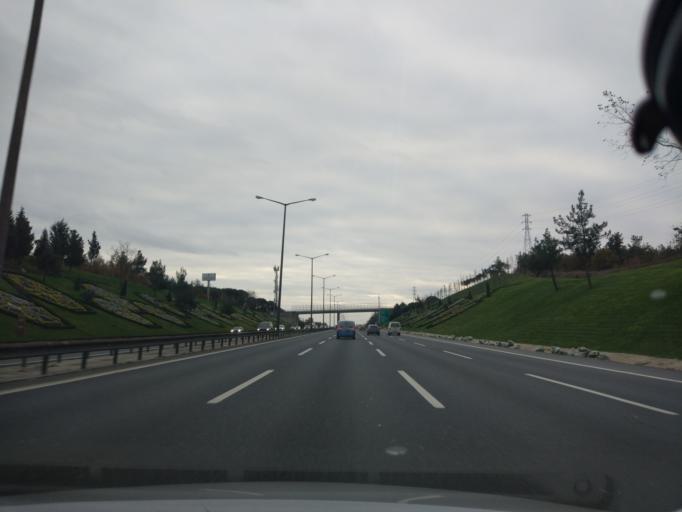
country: TR
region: Istanbul
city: Umraniye
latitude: 41.0685
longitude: 29.1080
